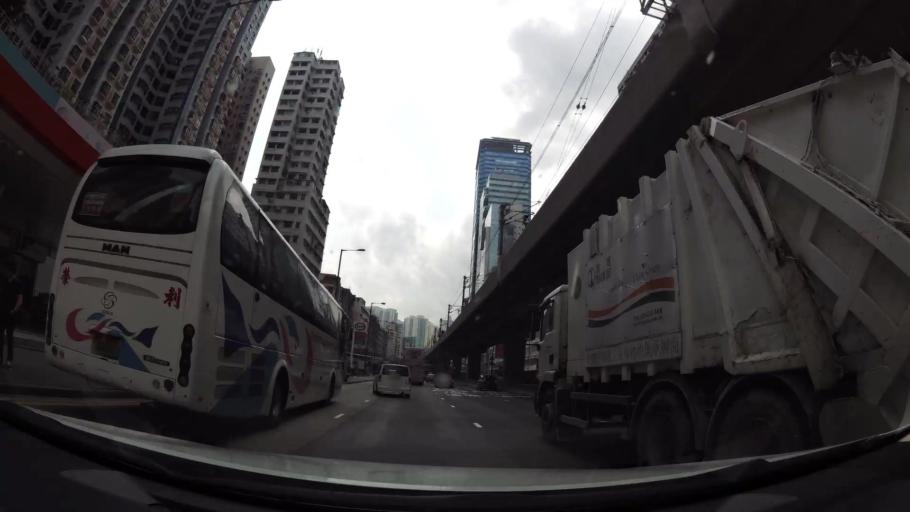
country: HK
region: Kowloon City
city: Kowloon
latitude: 22.3141
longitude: 114.2222
